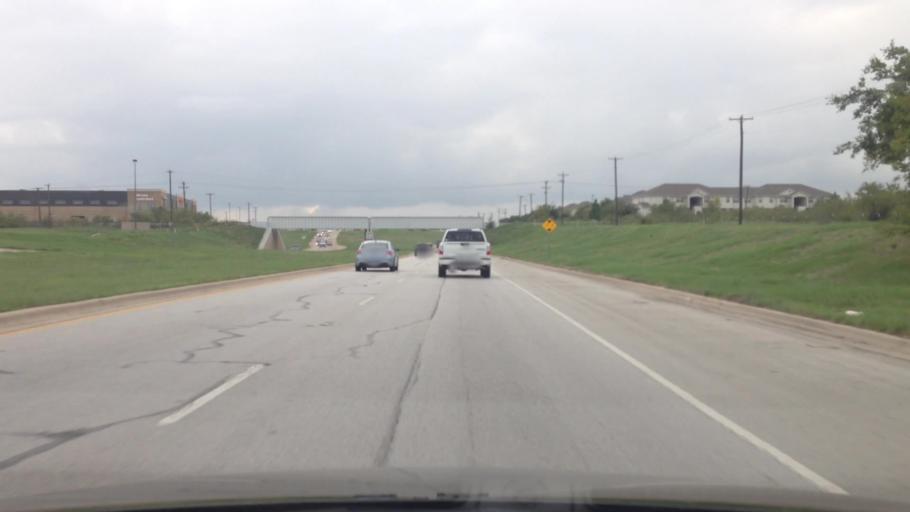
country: US
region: Texas
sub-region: Johnson County
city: Burleson
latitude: 32.5779
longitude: -97.3228
